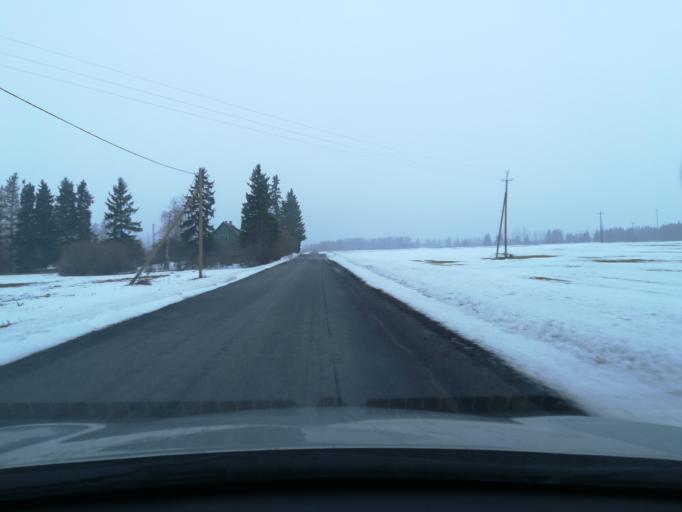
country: EE
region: Harju
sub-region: Raasiku vald
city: Raasiku
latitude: 59.3593
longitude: 25.1974
